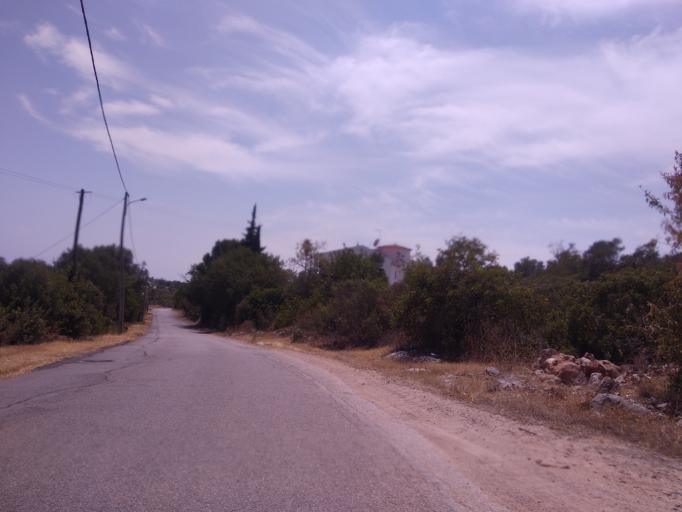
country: PT
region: Faro
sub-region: Faro
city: Santa Barbara de Nexe
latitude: 37.1077
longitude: -7.9519
